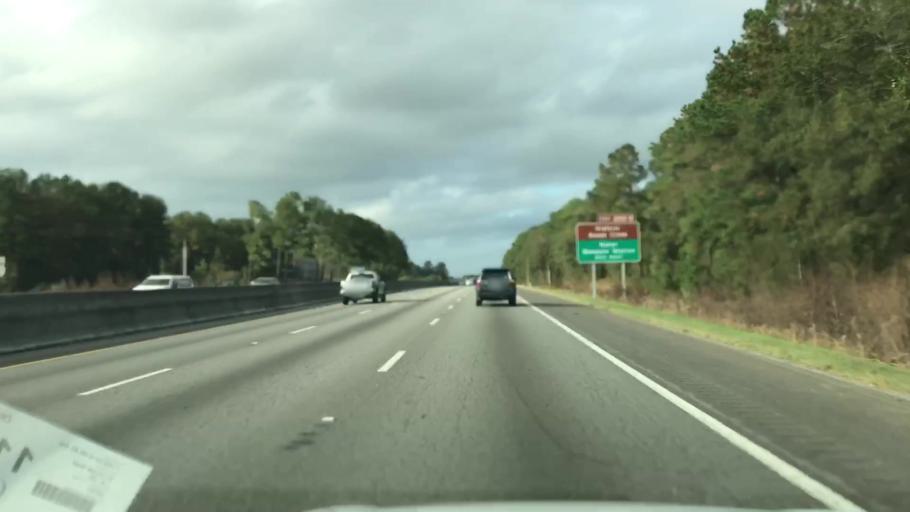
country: US
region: South Carolina
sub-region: Berkeley County
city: Ladson
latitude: 32.9713
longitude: -80.0756
